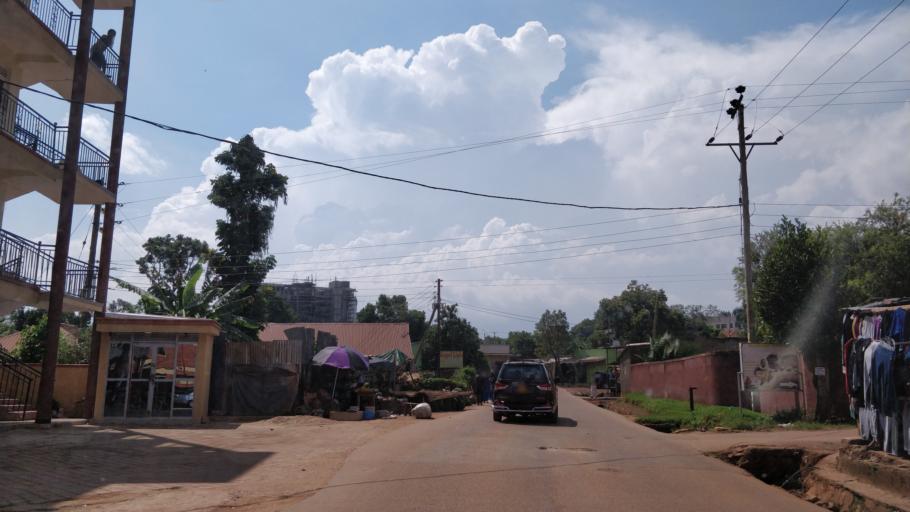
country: UG
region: Central Region
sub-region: Kampala District
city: Kampala
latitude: 0.2834
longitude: 32.6124
